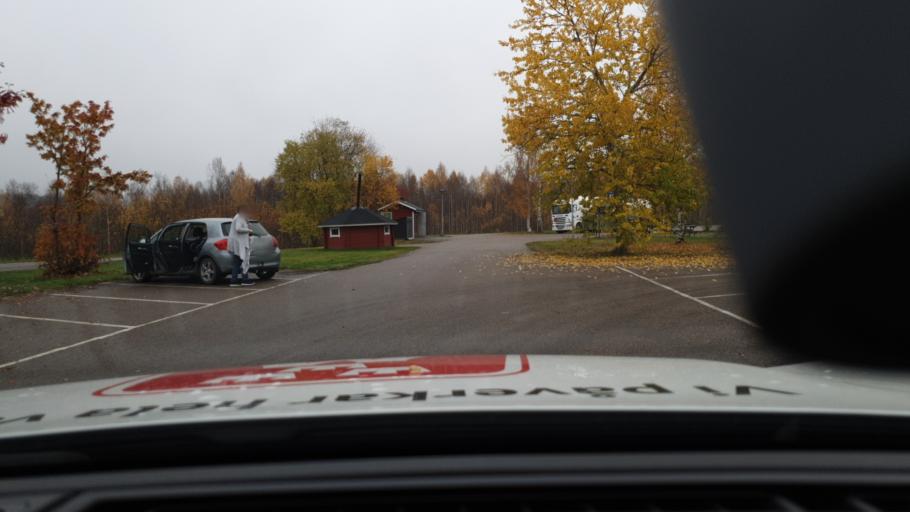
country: SE
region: Norrbotten
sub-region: Overkalix Kommun
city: OEverkalix
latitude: 66.6509
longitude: 22.1837
